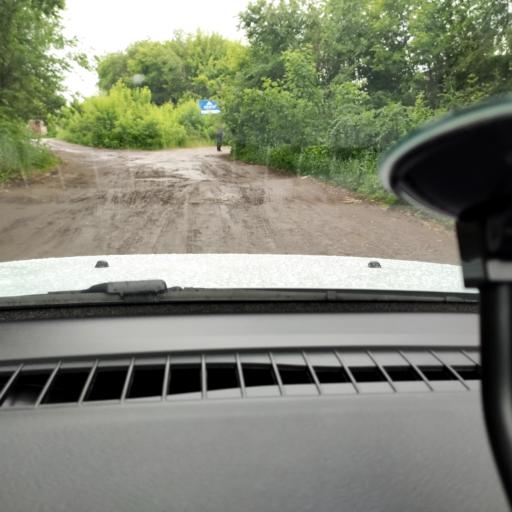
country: RU
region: Samara
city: Smyshlyayevka
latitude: 53.2197
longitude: 50.2836
